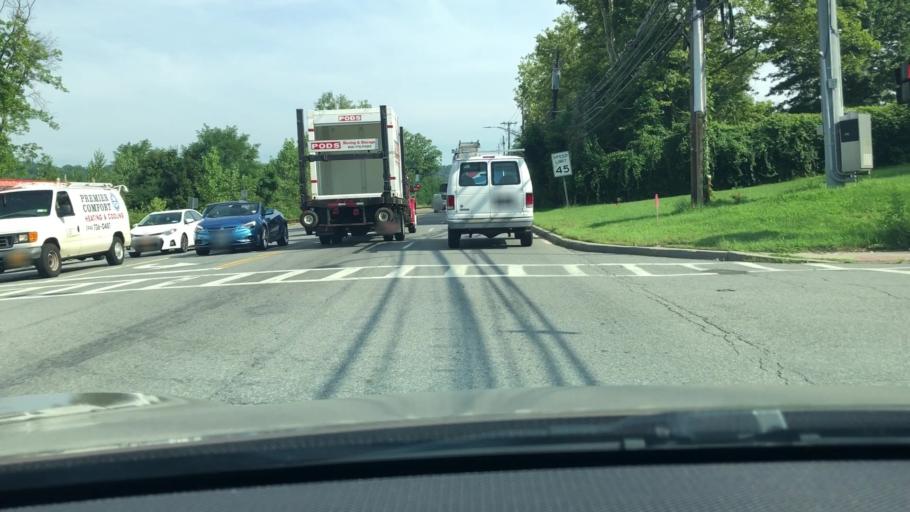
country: US
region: New York
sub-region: Westchester County
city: Elmsford
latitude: 41.0810
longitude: -73.8184
